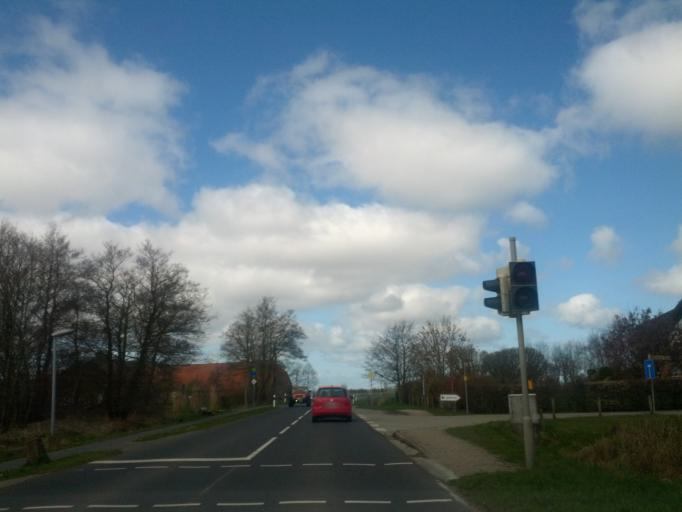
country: DE
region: Lower Saxony
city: Esens
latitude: 53.6546
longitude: 7.6082
